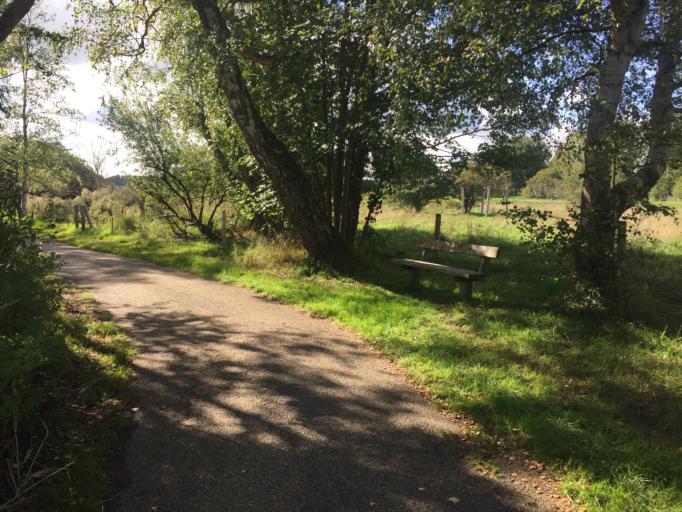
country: DK
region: Capital Region
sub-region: Herlev Kommune
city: Herlev
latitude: 55.7503
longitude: 12.4381
